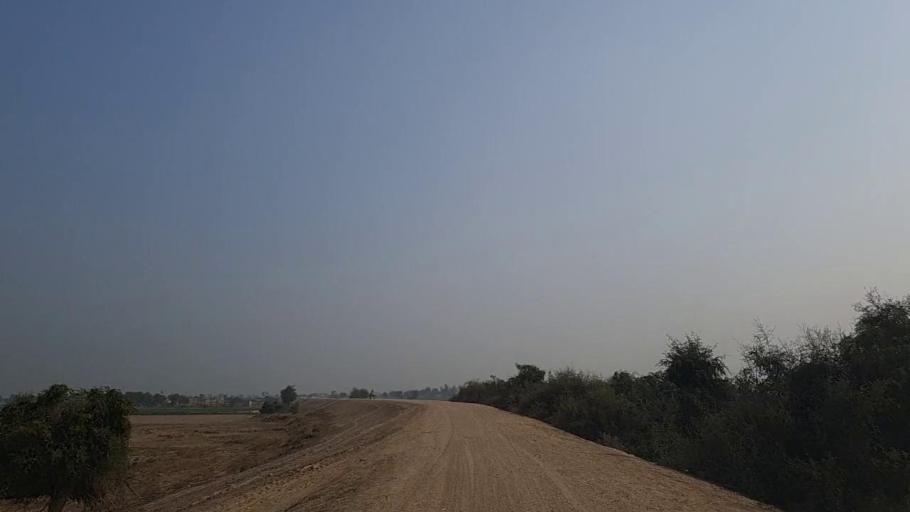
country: PK
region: Sindh
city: Sann
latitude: 26.0939
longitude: 68.1474
